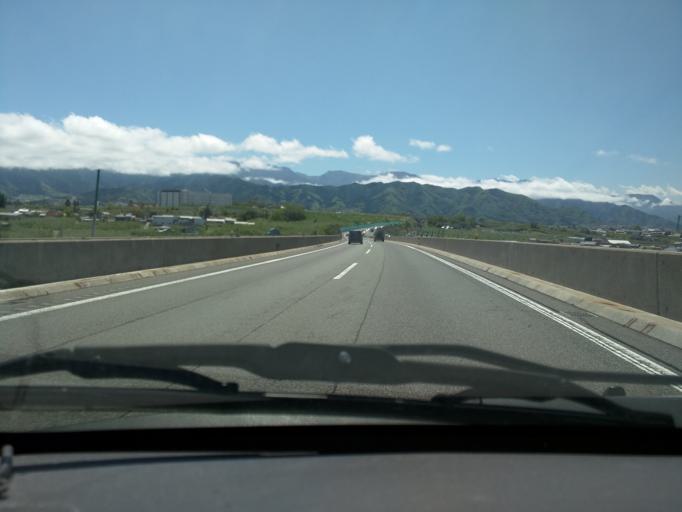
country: JP
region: Nagano
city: Nakano
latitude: 36.7442
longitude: 138.3131
